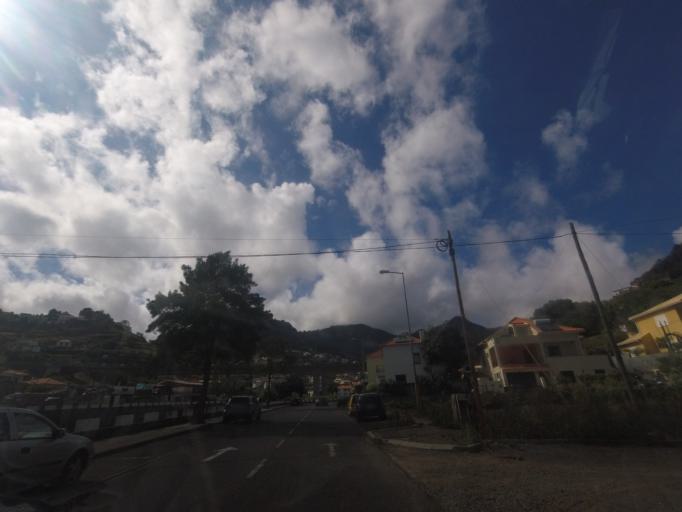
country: PT
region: Madeira
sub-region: Machico
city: Machico
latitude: 32.7306
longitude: -16.7760
